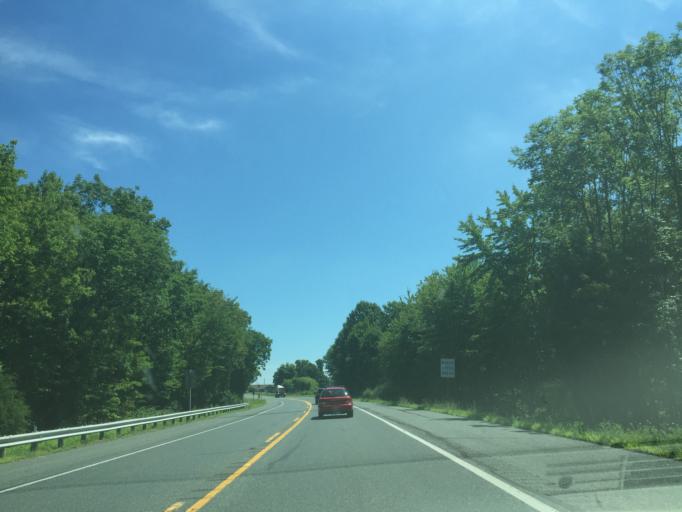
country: US
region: Maryland
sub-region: Harford County
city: Bel Air North
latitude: 39.5711
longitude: -76.3611
